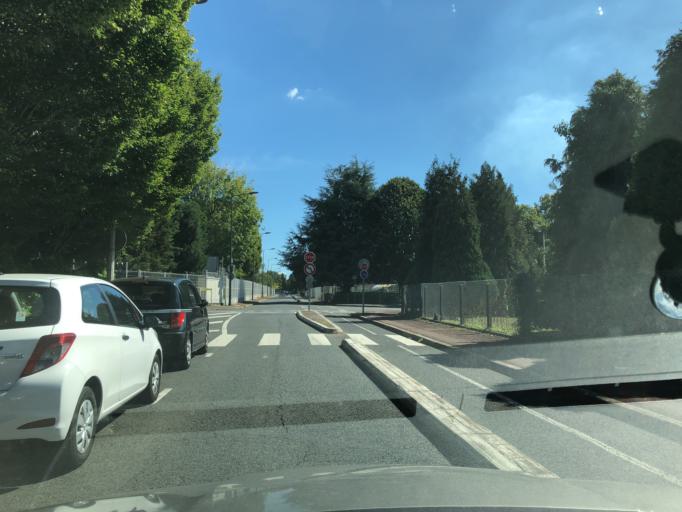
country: FR
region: Centre
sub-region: Departement d'Indre-et-Loire
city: Saint-Cyr-sur-Loire
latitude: 47.4290
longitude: 0.6832
